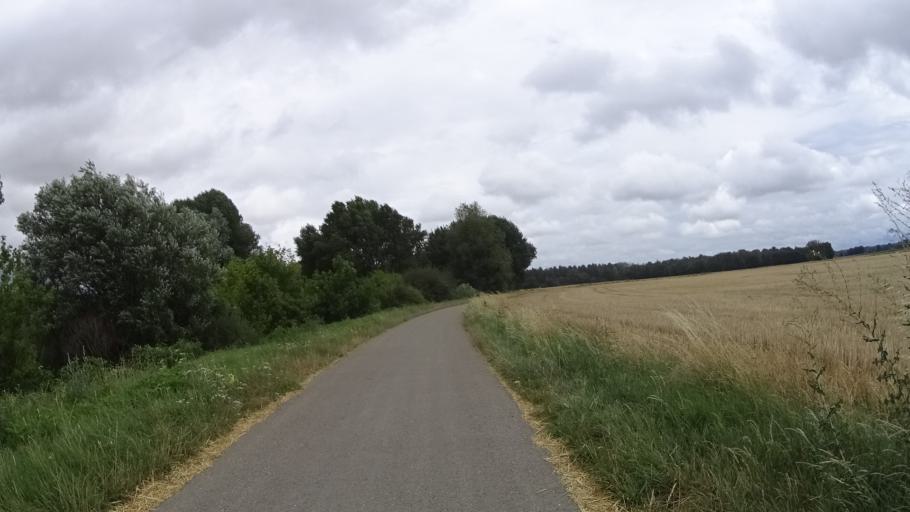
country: FR
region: Centre
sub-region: Departement du Loiret
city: Meung-sur-Loire
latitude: 47.8349
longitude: 1.7203
